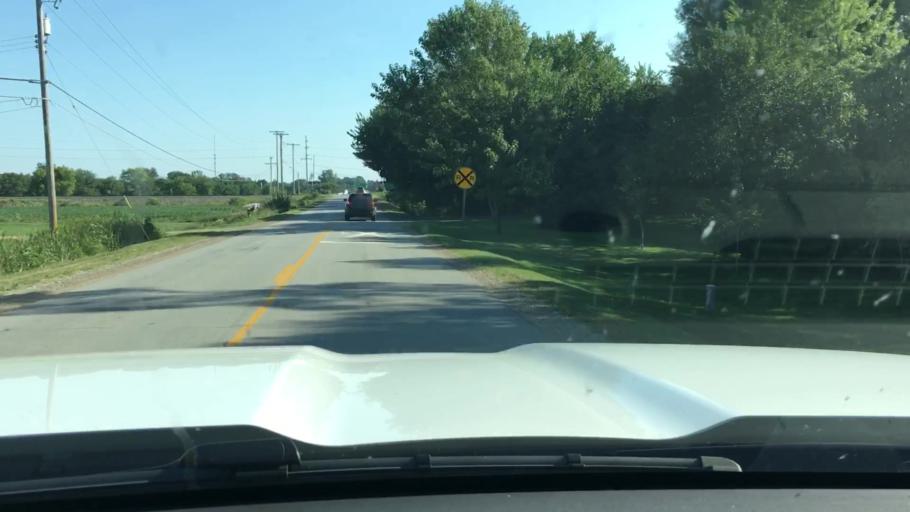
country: US
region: Michigan
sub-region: Ottawa County
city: Zeeland
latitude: 42.8353
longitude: -85.9598
